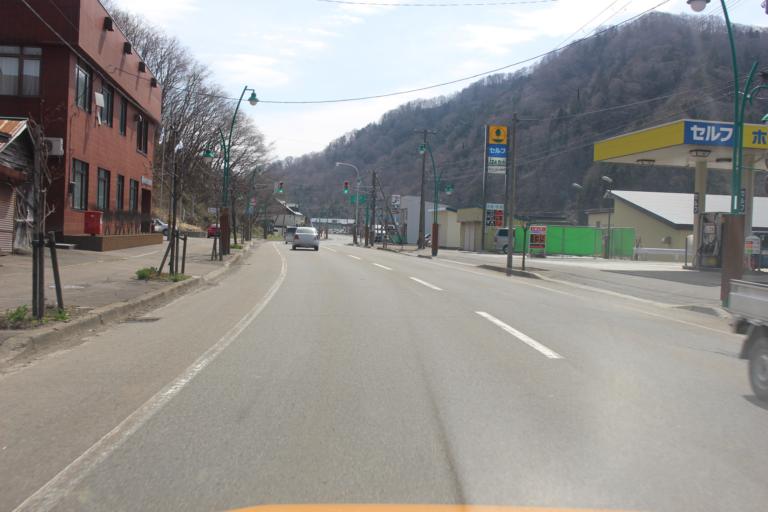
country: JP
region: Hokkaido
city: Kamiiso
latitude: 41.9155
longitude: 140.2256
